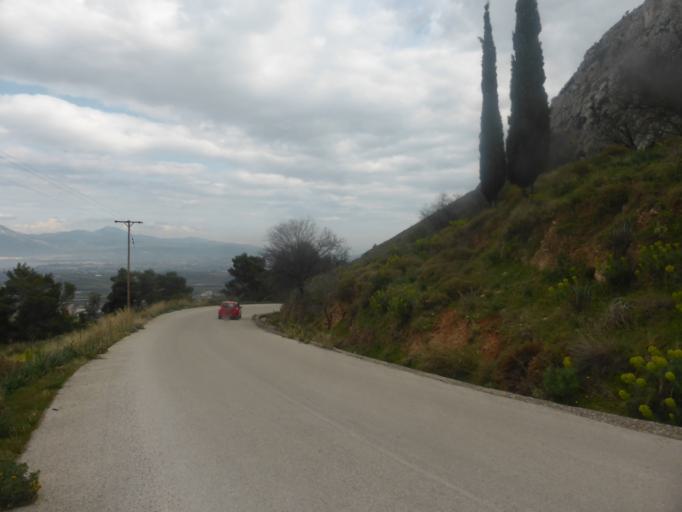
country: GR
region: Peloponnese
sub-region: Nomos Korinthias
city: Arkhaia Korinthos
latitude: 37.8970
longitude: 22.8706
